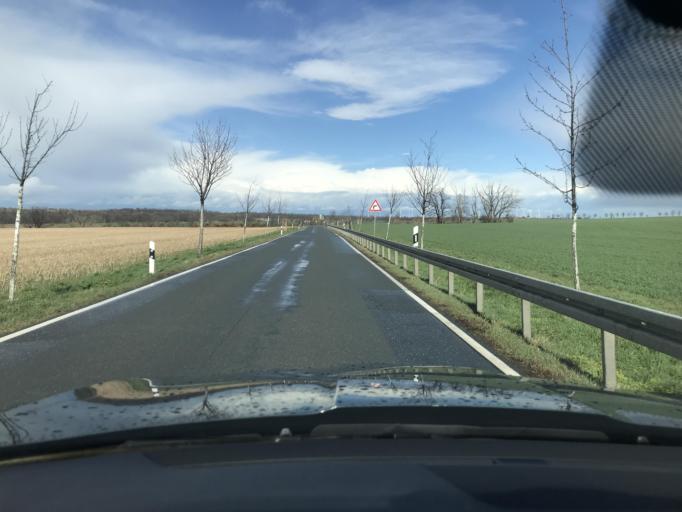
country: DE
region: Saxony-Anhalt
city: Hoym
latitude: 51.7160
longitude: 11.3102
